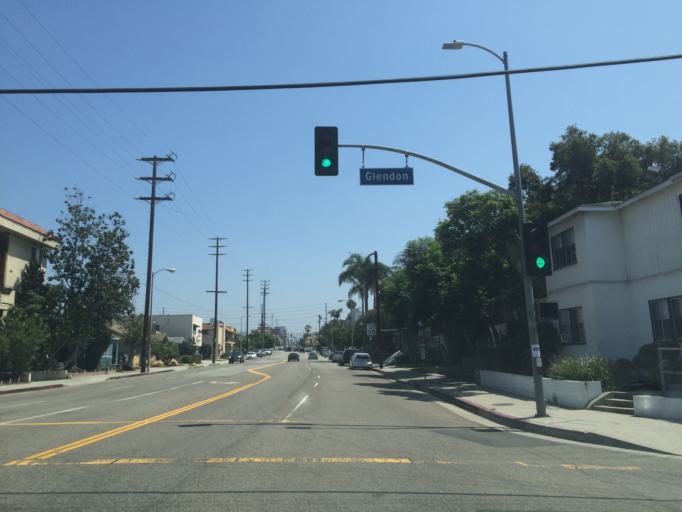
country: US
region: California
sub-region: Los Angeles County
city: Culver City
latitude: 34.0233
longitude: -118.4141
